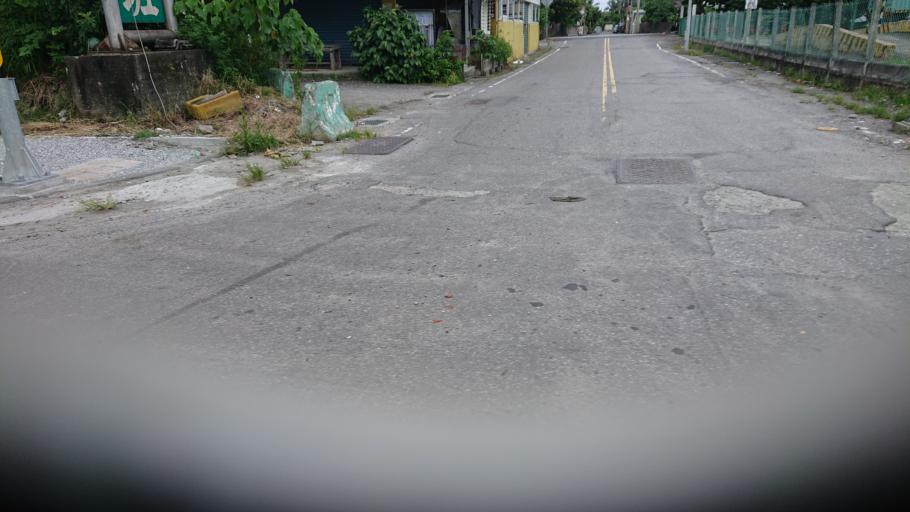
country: TW
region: Taiwan
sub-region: Hualien
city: Hualian
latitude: 23.9598
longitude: 121.6036
